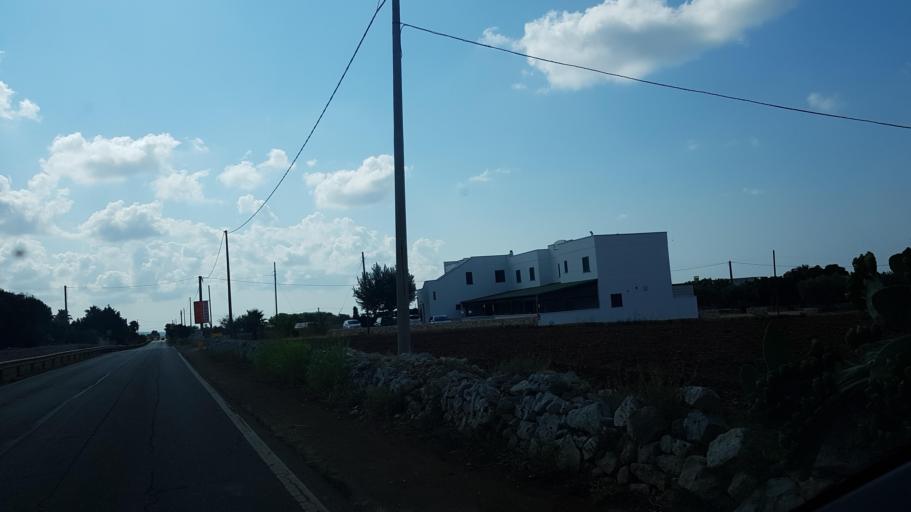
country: IT
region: Apulia
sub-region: Provincia di Lecce
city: Acquarica del Capo
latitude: 39.8429
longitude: 18.2160
